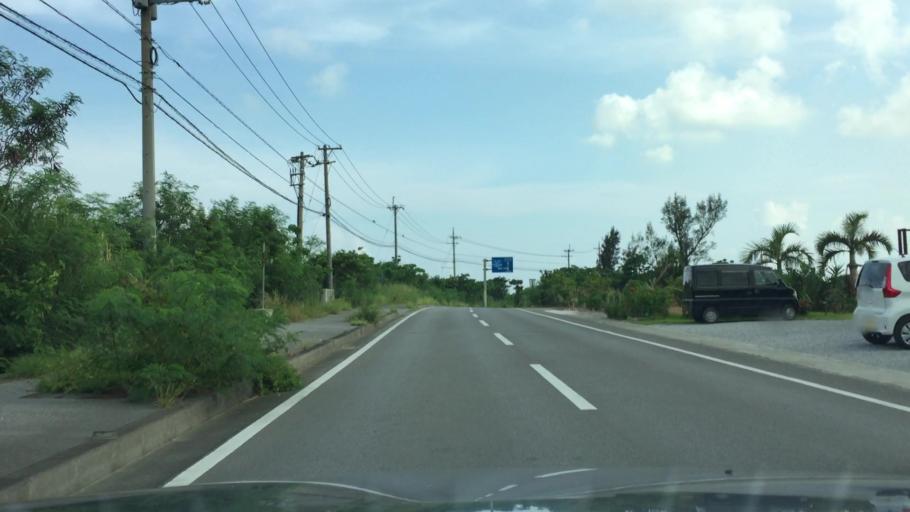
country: JP
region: Okinawa
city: Ishigaki
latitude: 24.3956
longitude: 124.1954
